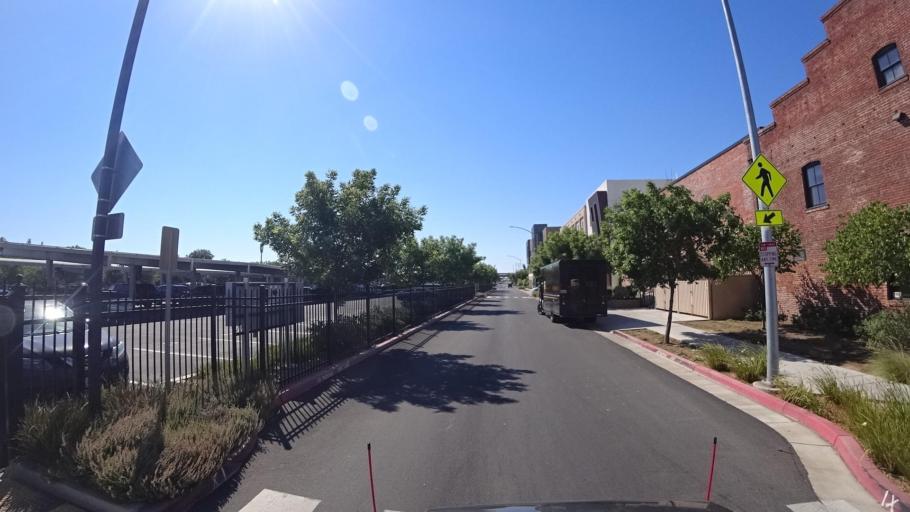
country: US
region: California
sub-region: Fresno County
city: Fresno
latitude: 36.7367
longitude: -119.7812
